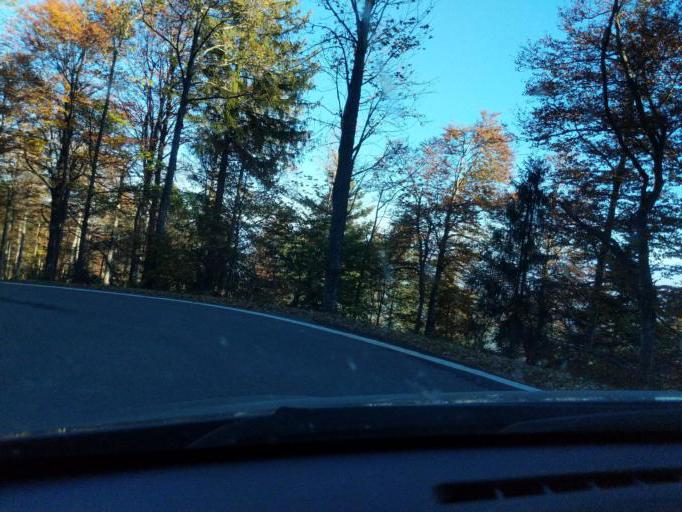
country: CH
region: Bern
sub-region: Jura bernois
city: Saint-Imier
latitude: 47.1108
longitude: 7.0317
